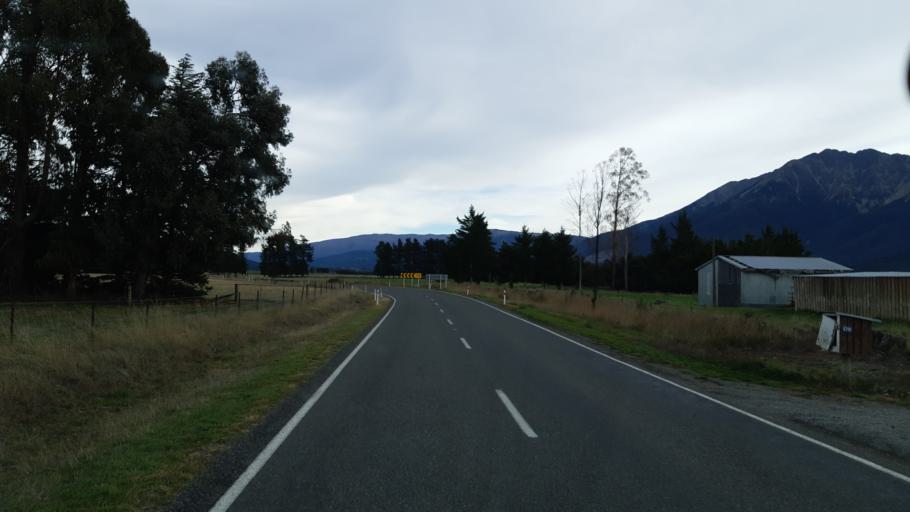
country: NZ
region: Tasman
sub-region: Tasman District
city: Brightwater
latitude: -41.6384
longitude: 173.3150
